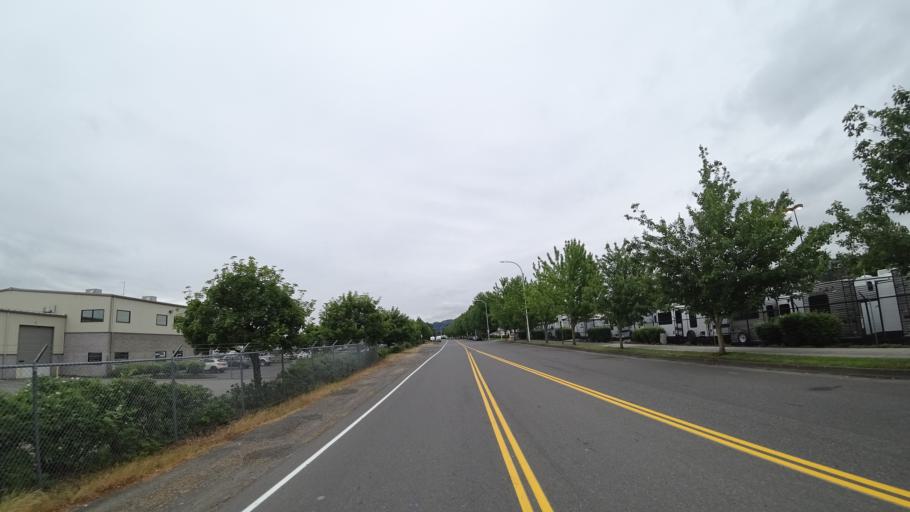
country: US
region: Oregon
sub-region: Multnomah County
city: Wood Village
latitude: 45.5427
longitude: -122.4170
